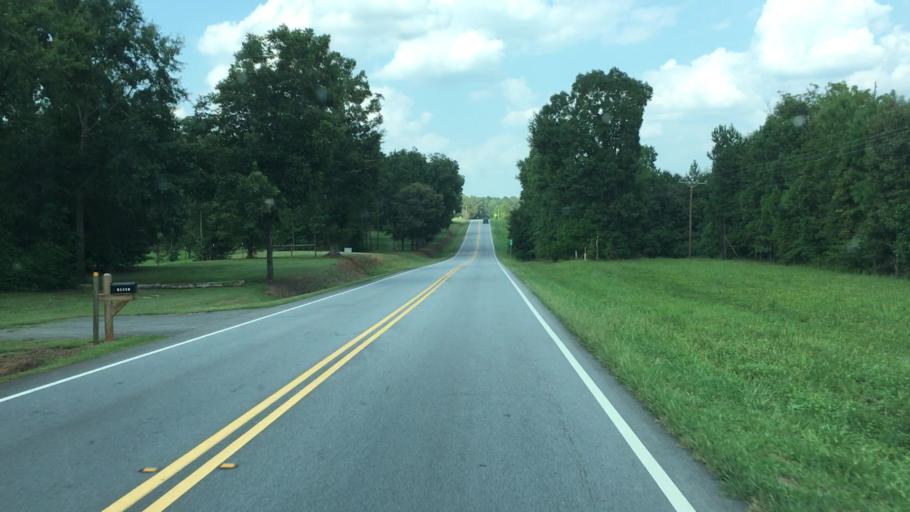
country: US
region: Georgia
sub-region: Jasper County
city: Monticello
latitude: 33.3768
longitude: -83.7517
